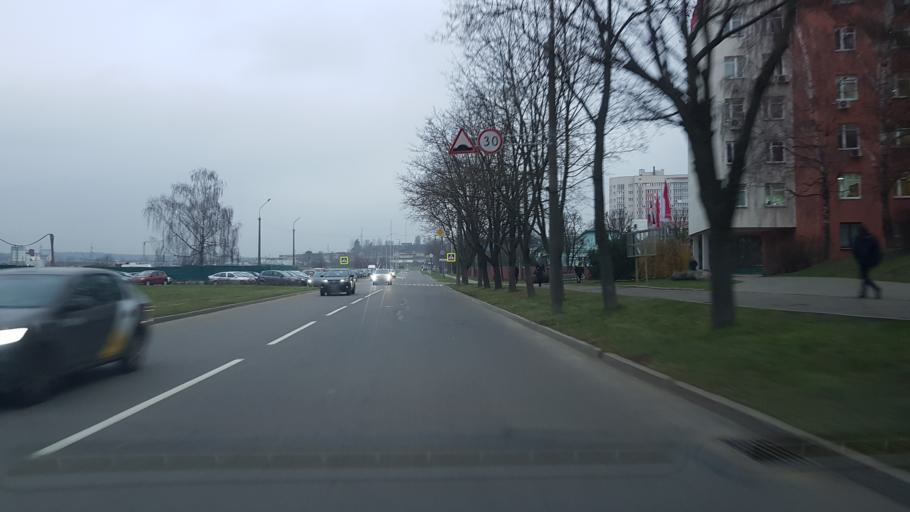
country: BY
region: Minsk
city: Minsk
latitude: 53.9343
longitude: 27.5365
